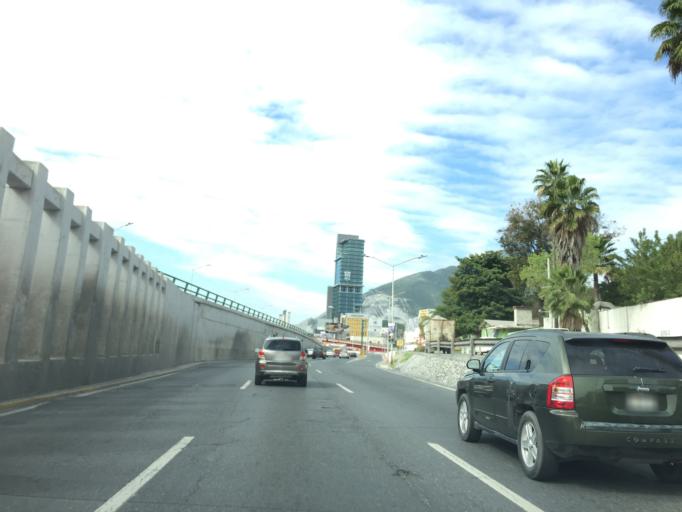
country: MX
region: Nuevo Leon
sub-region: Monterrey
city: Monterrey
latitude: 25.6717
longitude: -100.3492
